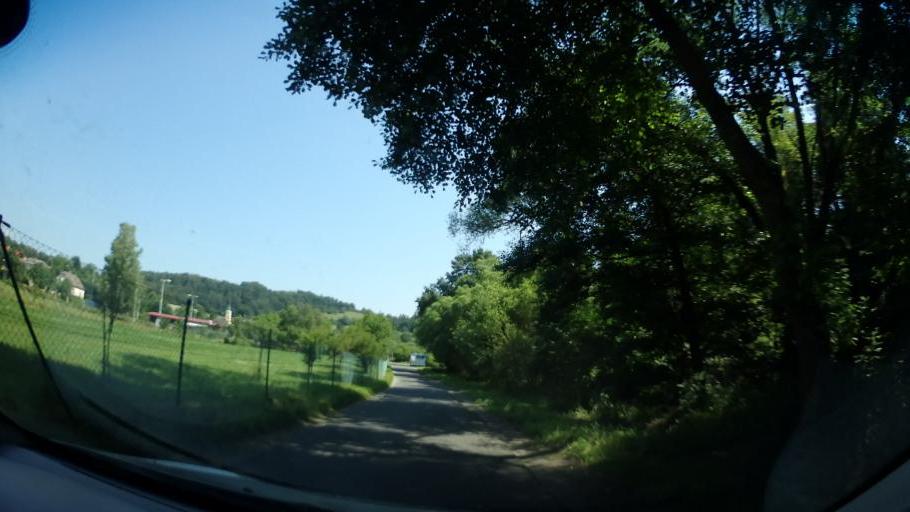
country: CZ
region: Olomoucky
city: Zabreh
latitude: 49.8639
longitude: 16.8161
